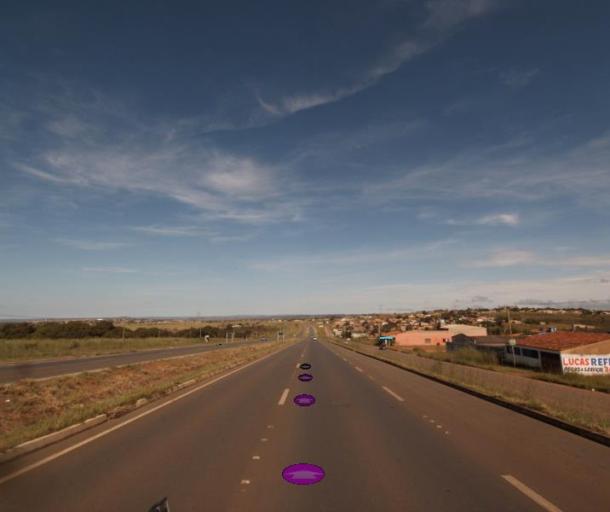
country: BR
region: Federal District
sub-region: Brasilia
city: Brasilia
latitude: -15.7392
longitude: -48.3034
